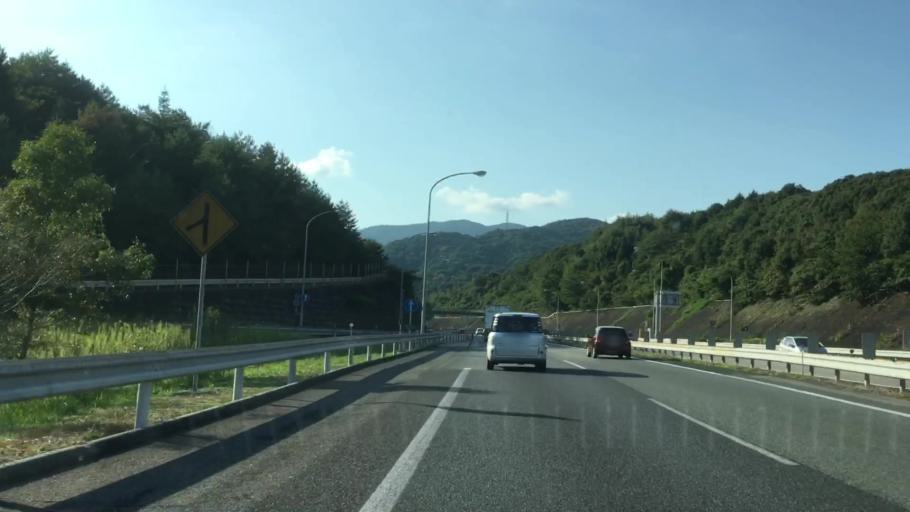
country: JP
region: Yamaguchi
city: Hofu
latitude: 34.0700
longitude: 131.6849
